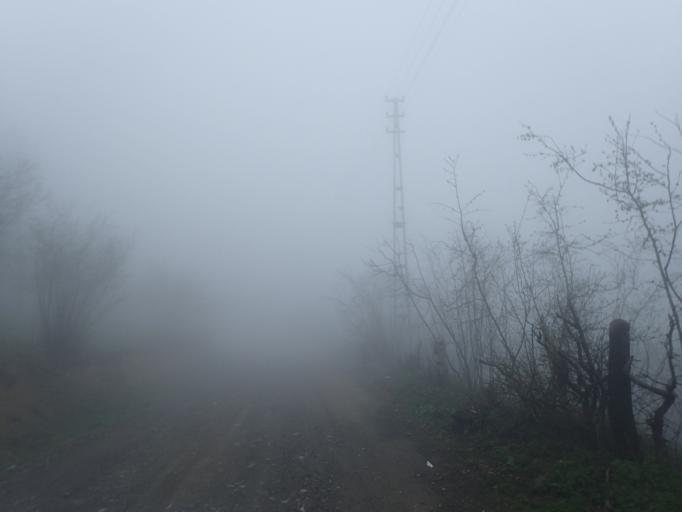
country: TR
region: Ordu
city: Korgan
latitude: 40.7831
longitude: 37.2887
